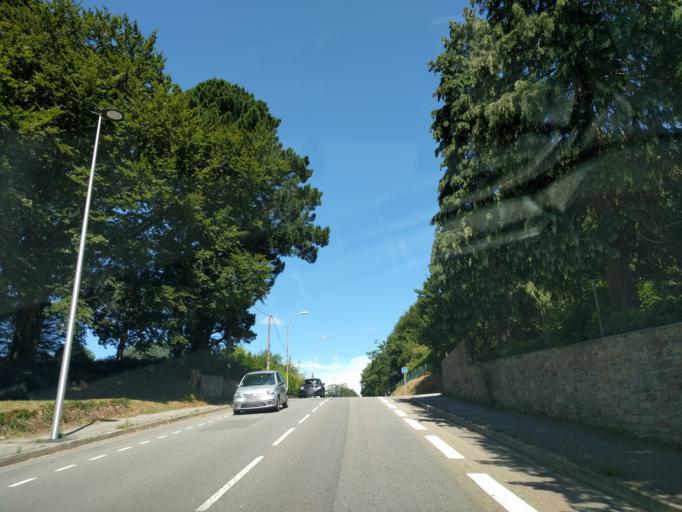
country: FR
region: Brittany
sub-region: Departement du Finistere
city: Quimper
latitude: 47.9827
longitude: -4.0974
